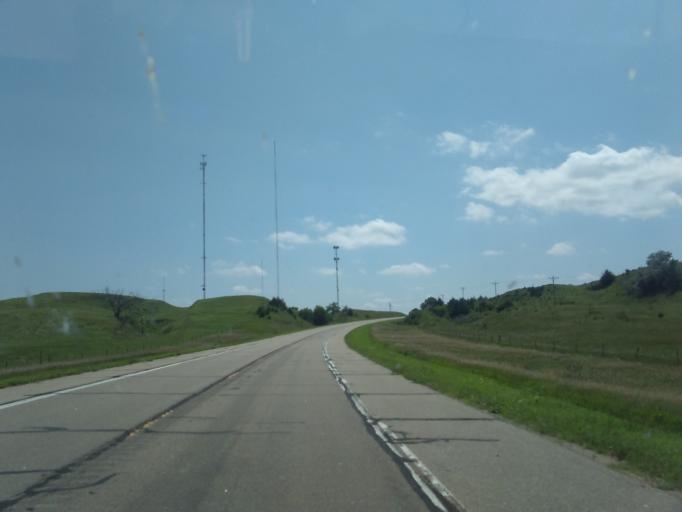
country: US
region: Nebraska
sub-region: Dawson County
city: Lexington
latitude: 40.7051
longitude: -99.7874
